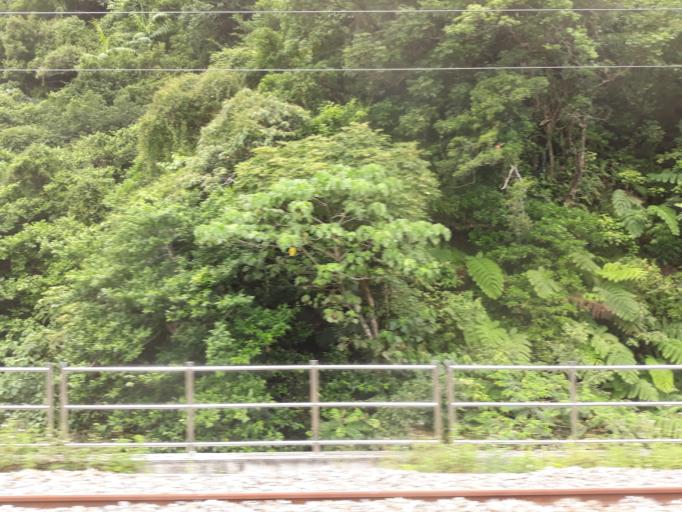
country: TW
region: Taiwan
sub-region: Yilan
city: Yilan
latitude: 24.4465
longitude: 121.7765
